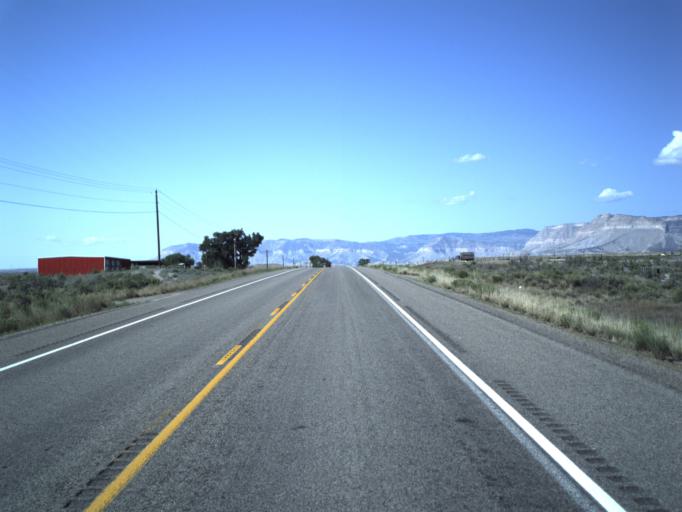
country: US
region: Utah
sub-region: Emery County
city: Castle Dale
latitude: 39.1881
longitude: -111.0288
